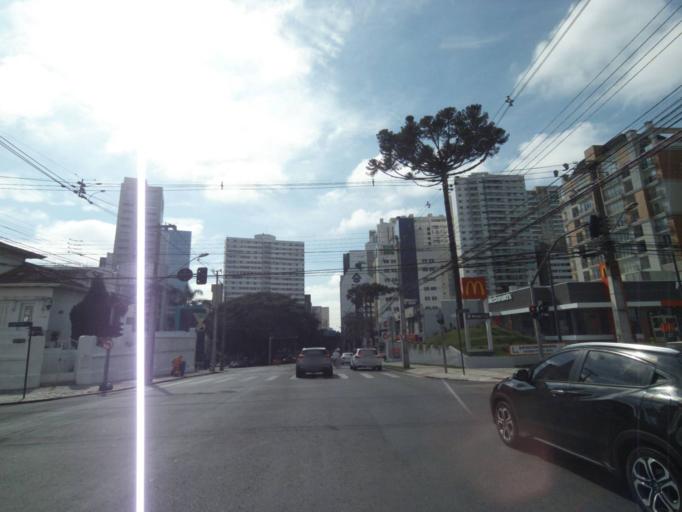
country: BR
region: Parana
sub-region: Curitiba
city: Curitiba
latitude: -25.4395
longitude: -49.2803
